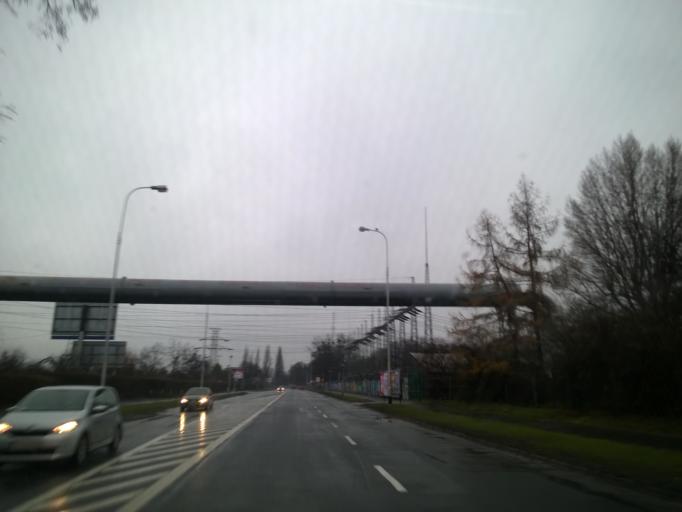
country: PL
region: Lower Silesian Voivodeship
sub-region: Powiat wroclawski
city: Wroclaw
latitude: 51.1228
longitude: 17.0117
